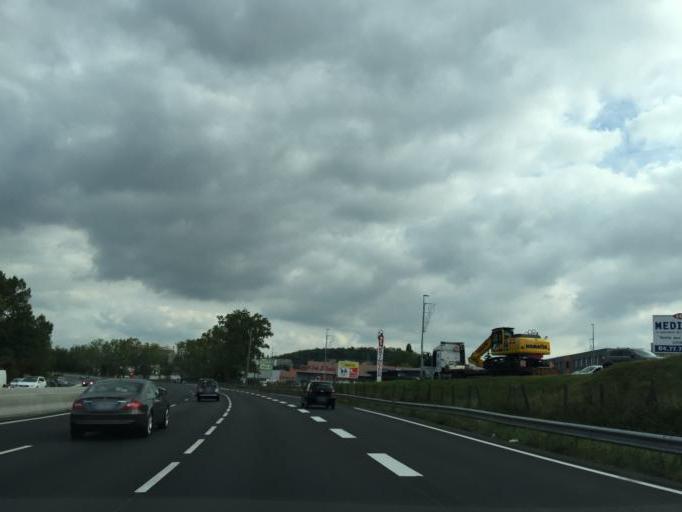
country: FR
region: Rhone-Alpes
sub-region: Departement de la Loire
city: Villars
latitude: 45.4701
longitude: 4.3657
